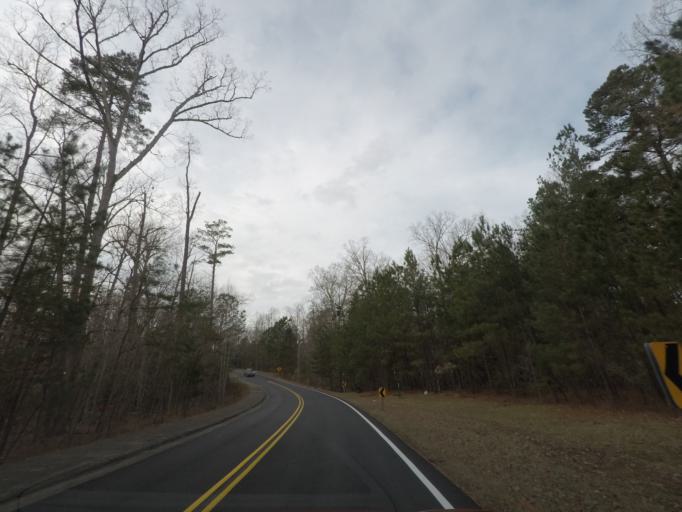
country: US
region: North Carolina
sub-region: Durham County
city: Durham
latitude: 36.0423
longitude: -78.9539
